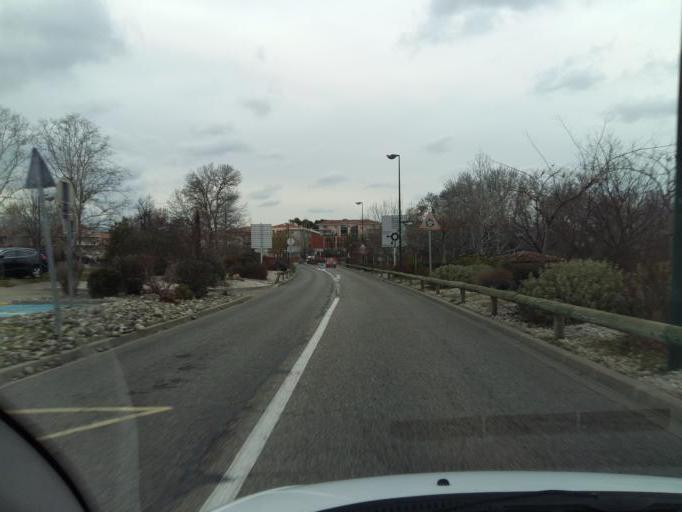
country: FR
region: Provence-Alpes-Cote d'Azur
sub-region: Departement des Bouches-du-Rhone
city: Cabries
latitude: 43.4907
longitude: 5.3562
